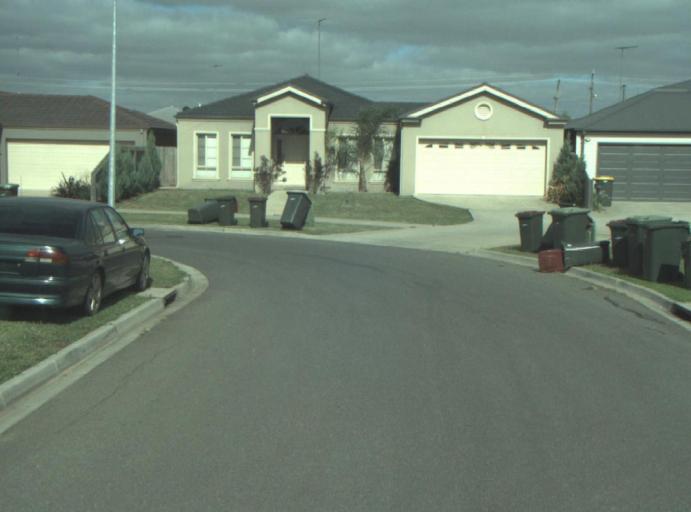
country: AU
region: Victoria
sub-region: Greater Geelong
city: Wandana Heights
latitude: -38.2135
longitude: 144.3030
